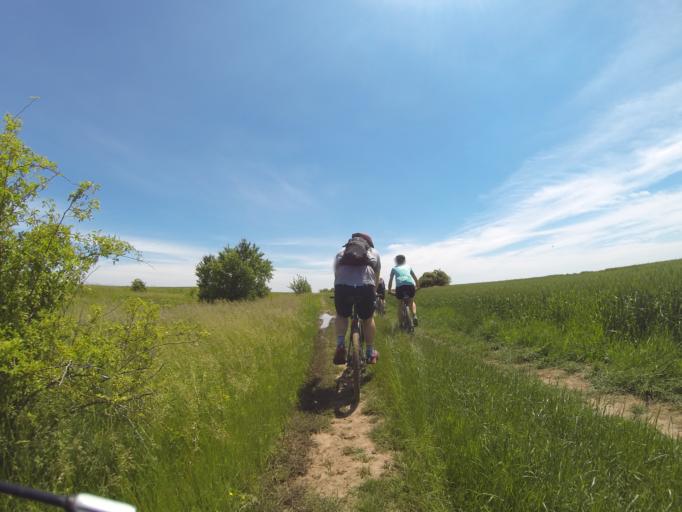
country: RO
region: Dolj
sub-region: Comuna Leu
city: Zanoaga
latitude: 44.1812
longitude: 24.0760
